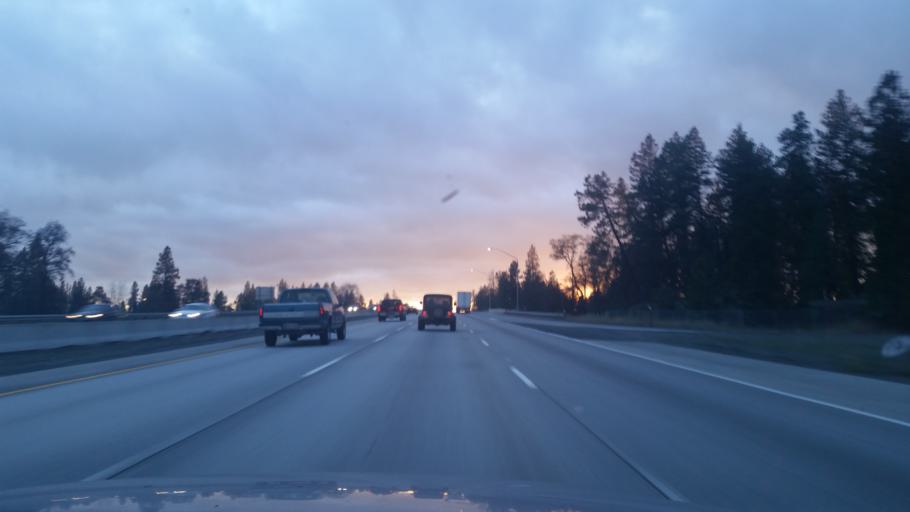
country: US
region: Washington
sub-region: Spokane County
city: Spokane
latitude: 47.6328
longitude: -117.4817
